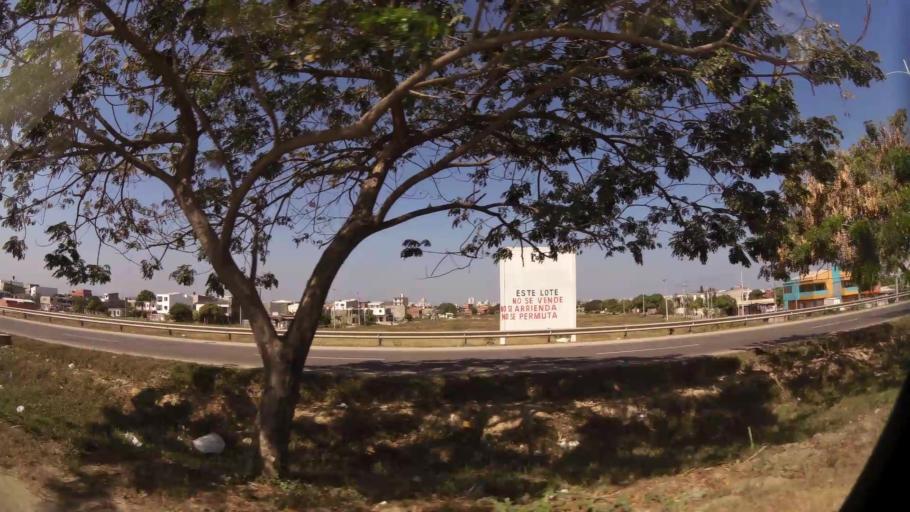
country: CO
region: Bolivar
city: Cartagena
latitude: 10.3857
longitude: -75.4499
